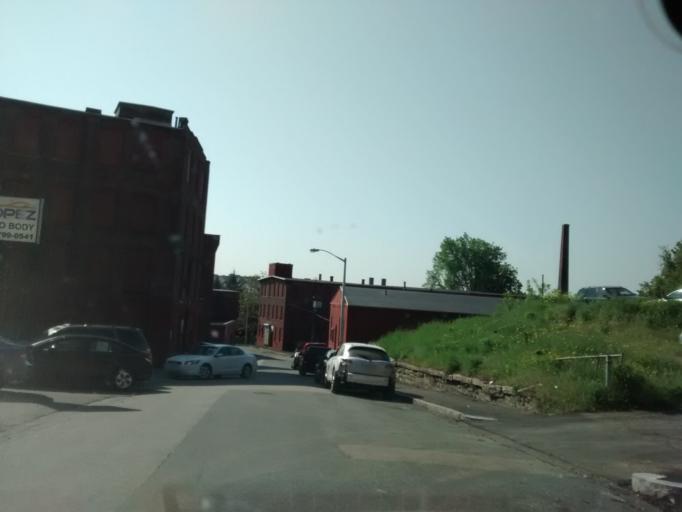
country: US
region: Massachusetts
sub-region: Worcester County
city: Worcester
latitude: 42.2548
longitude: -71.8087
